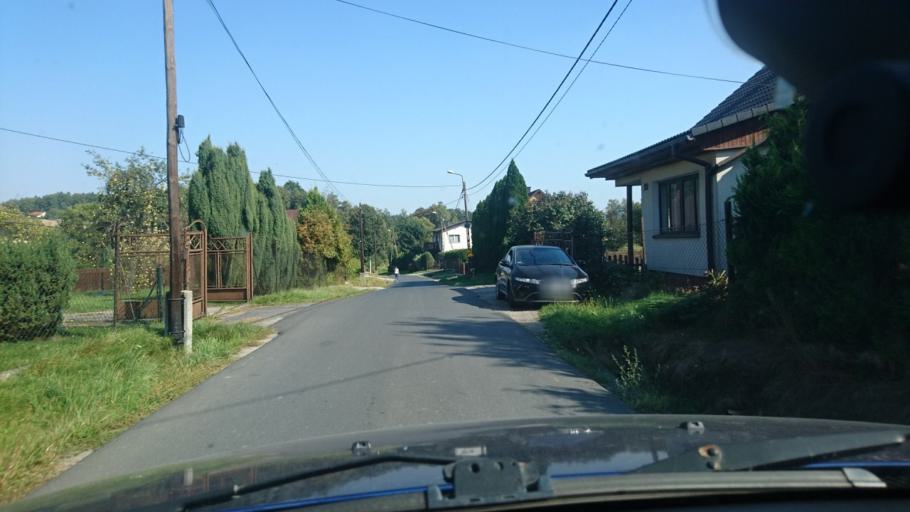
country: PL
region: Silesian Voivodeship
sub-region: Bielsko-Biala
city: Bielsko-Biala
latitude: 49.8577
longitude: 19.0612
